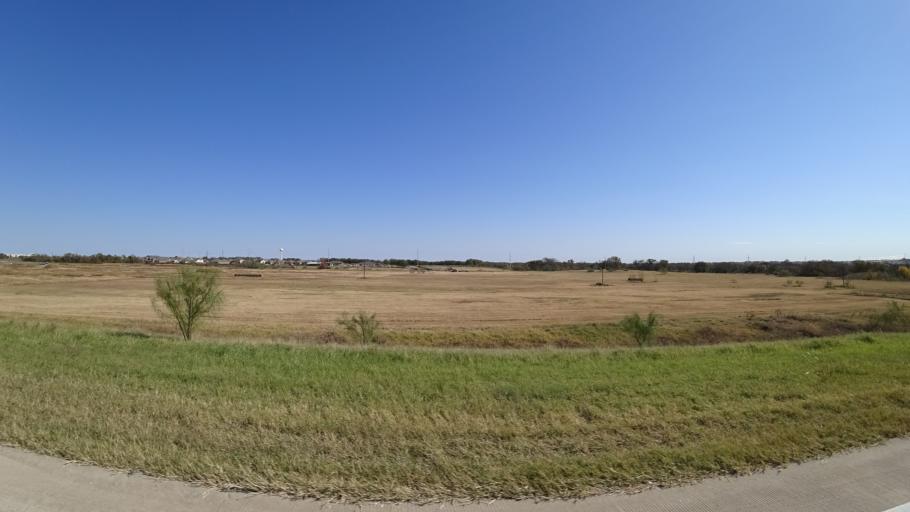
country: US
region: Texas
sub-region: Williamson County
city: Hutto
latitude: 30.5299
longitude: -97.5754
